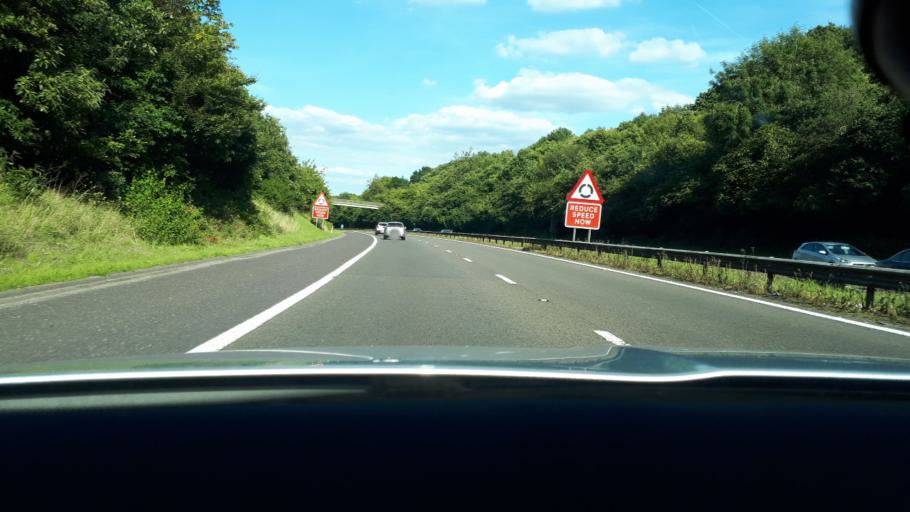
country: GB
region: England
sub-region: Kent
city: Halstead
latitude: 51.3459
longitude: 0.1477
